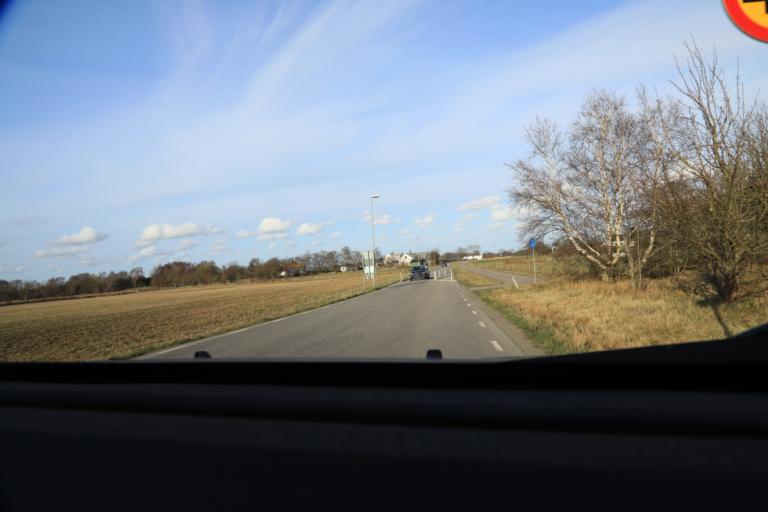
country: SE
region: Halland
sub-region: Varbergs Kommun
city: Varberg
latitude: 57.1198
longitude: 12.2167
